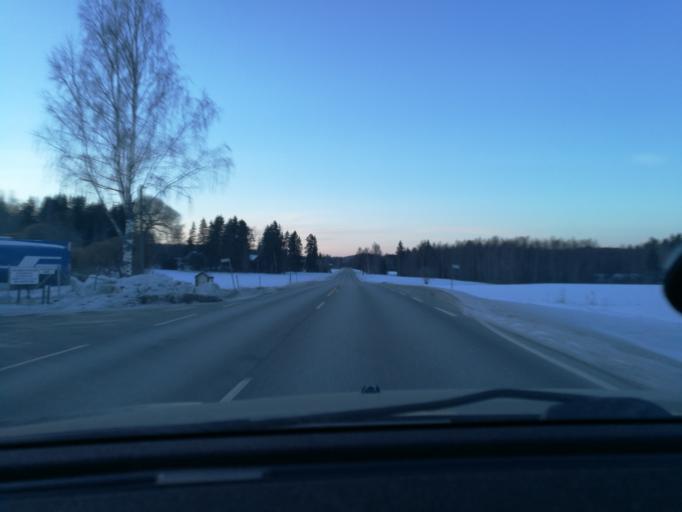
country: FI
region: Uusimaa
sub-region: Helsinki
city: Vihti
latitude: 60.4161
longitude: 24.4460
